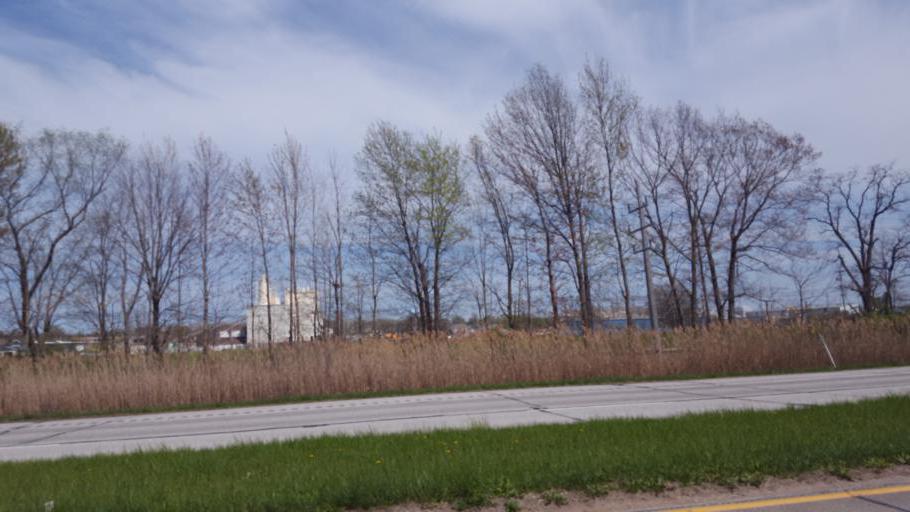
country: US
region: Ohio
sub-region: Lake County
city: Fairport Harbor
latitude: 41.7468
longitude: -81.2879
